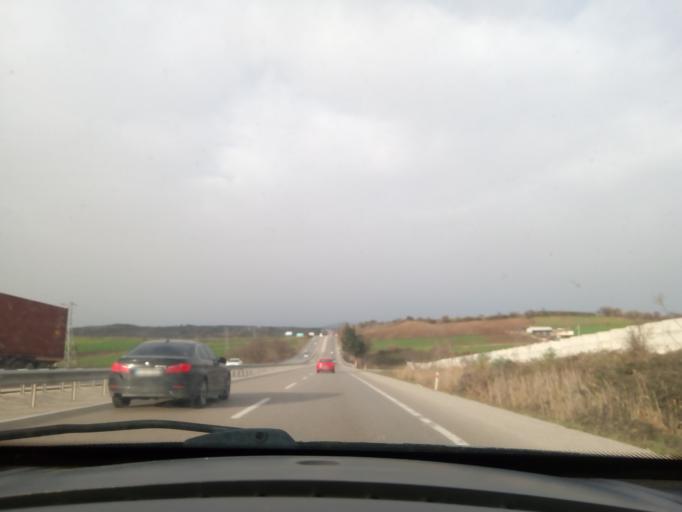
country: TR
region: Bursa
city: Mahmudiye
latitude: 40.2139
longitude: 28.6731
